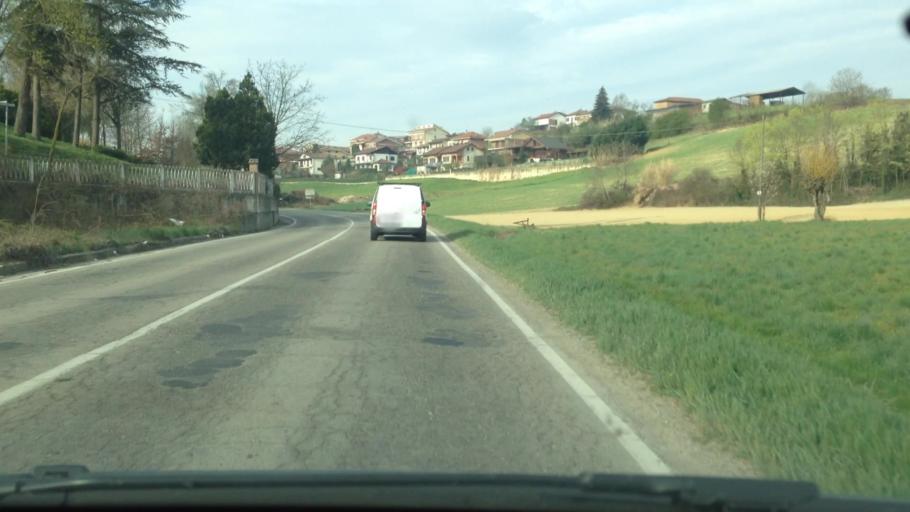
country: IT
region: Piedmont
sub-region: Provincia di Asti
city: San Damiano d'Asti
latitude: 44.8381
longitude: 8.0654
